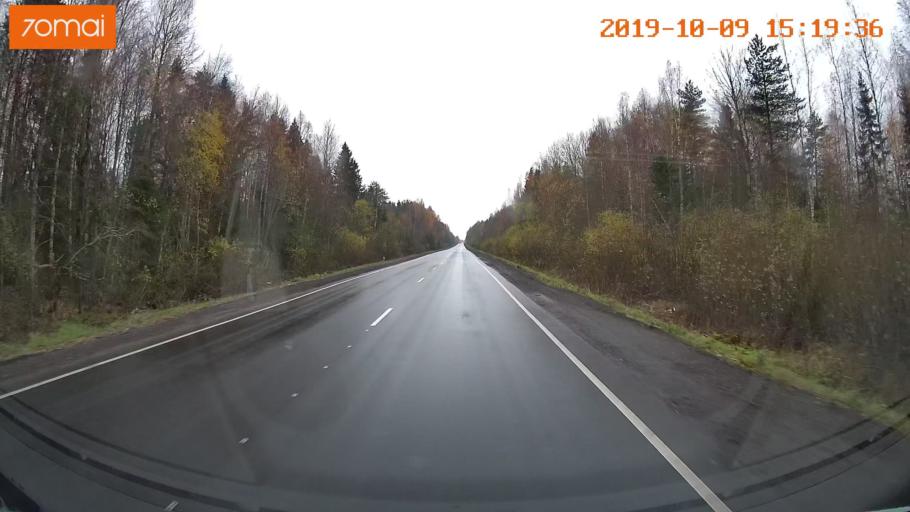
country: RU
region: Kostroma
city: Susanino
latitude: 58.0738
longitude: 41.5533
